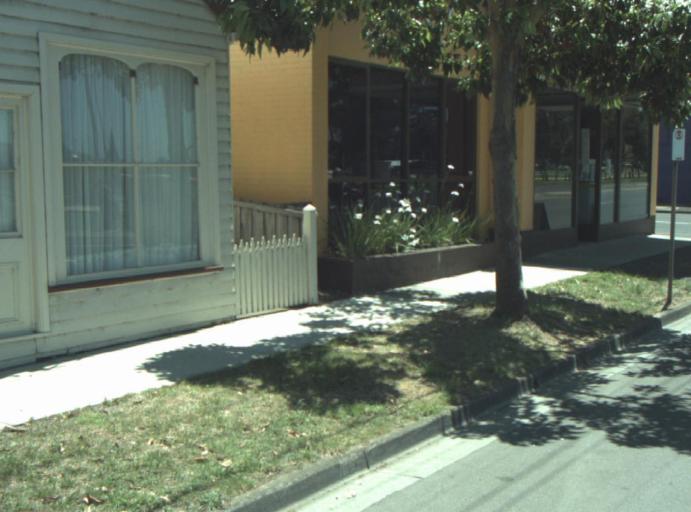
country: AU
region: Victoria
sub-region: Greater Geelong
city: Geelong
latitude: -38.1577
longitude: 144.3507
